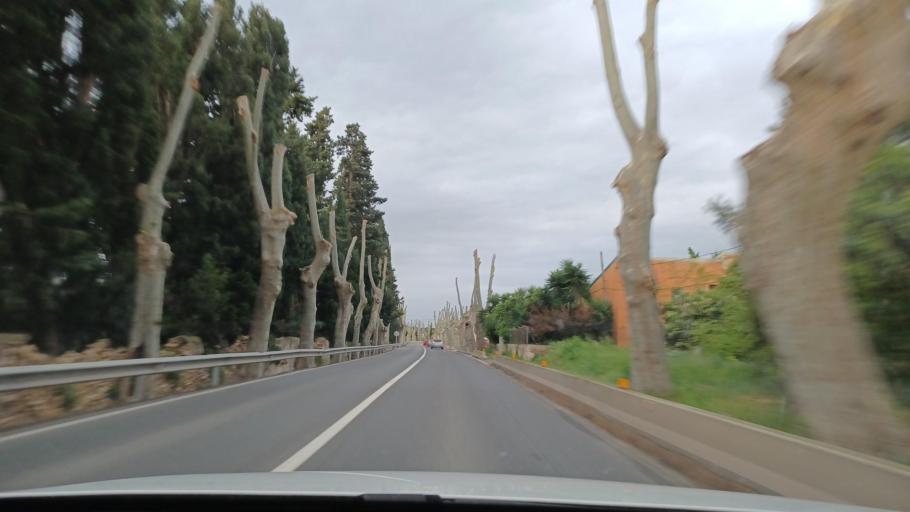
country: ES
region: Catalonia
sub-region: Provincia de Tarragona
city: Tortosa
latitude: 40.8043
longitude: 0.5045
